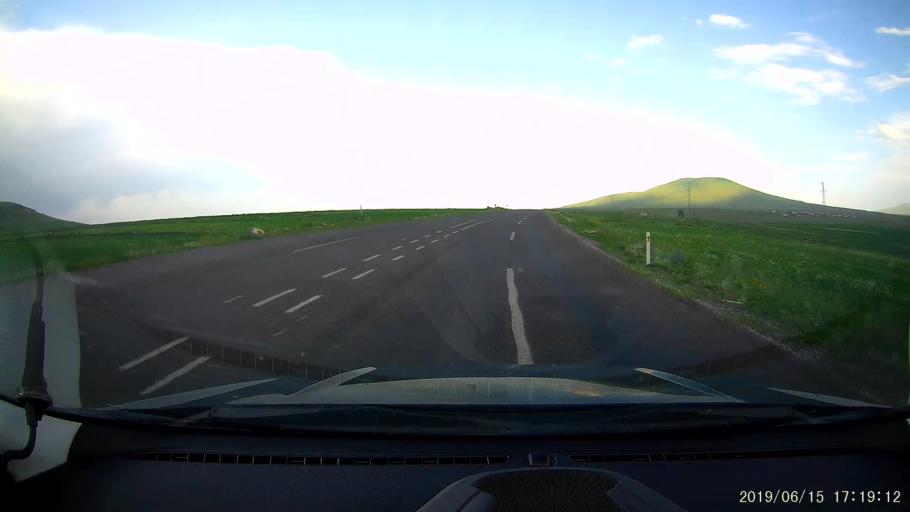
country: TR
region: Kars
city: Kars
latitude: 40.6165
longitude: 43.2733
